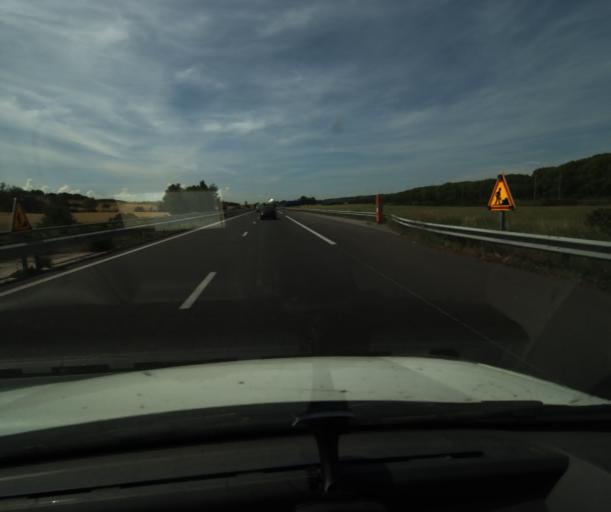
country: FR
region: Midi-Pyrenees
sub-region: Departement de la Haute-Garonne
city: Avignonet-Lauragais
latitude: 43.3422
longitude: 1.8265
